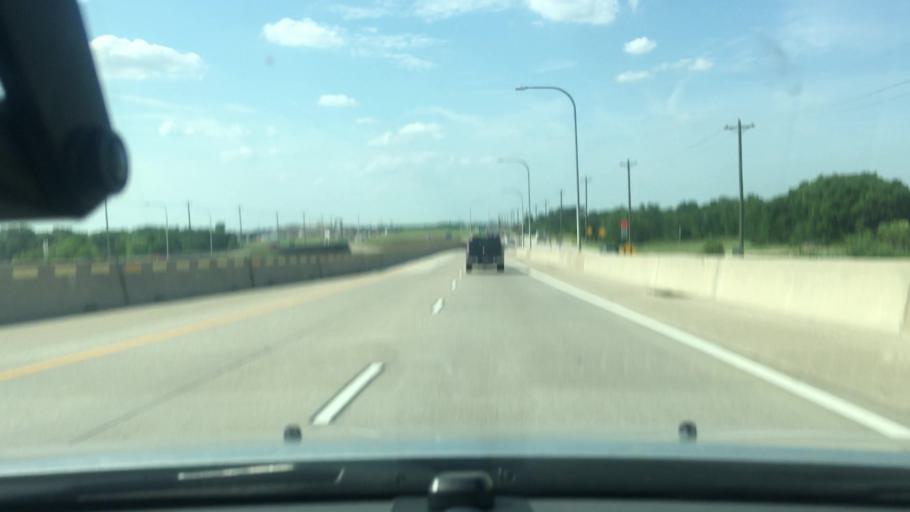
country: US
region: Texas
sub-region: Collin County
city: Prosper
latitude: 33.2107
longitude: -96.8198
